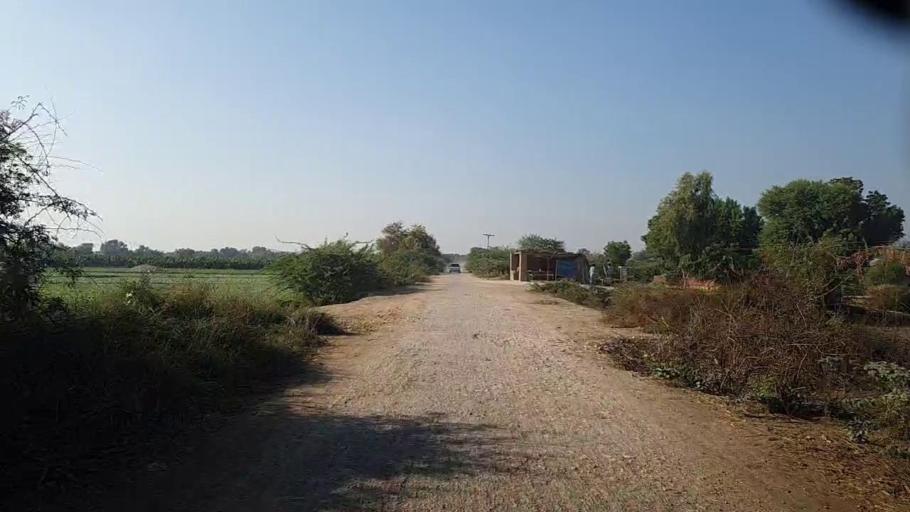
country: PK
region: Sindh
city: Darya Khan Marri
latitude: 26.6761
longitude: 68.3764
